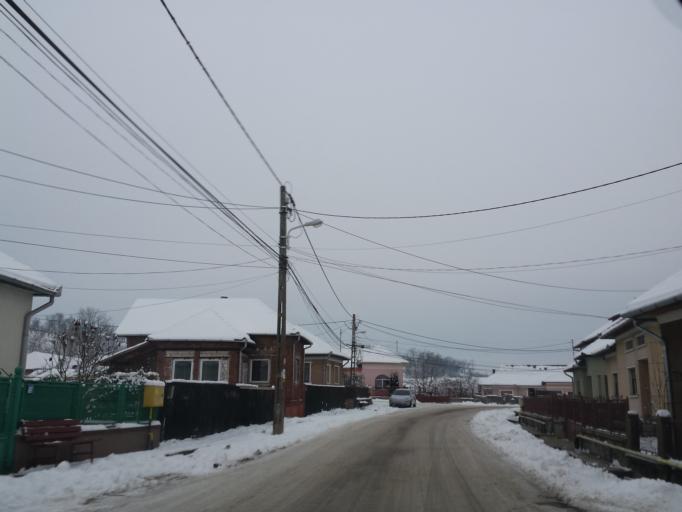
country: RO
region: Hunedoara
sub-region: Municipiul Deva
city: Cristur
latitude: 45.8283
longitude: 22.9412
